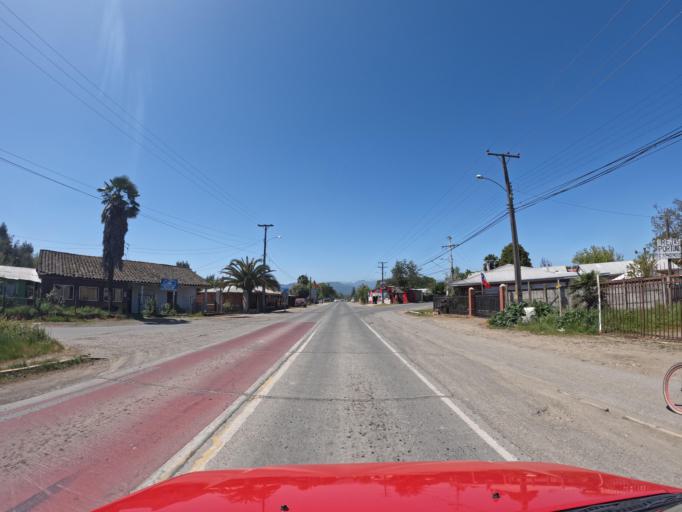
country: CL
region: Maule
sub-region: Provincia de Linares
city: Linares
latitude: -35.8302
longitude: -71.5121
